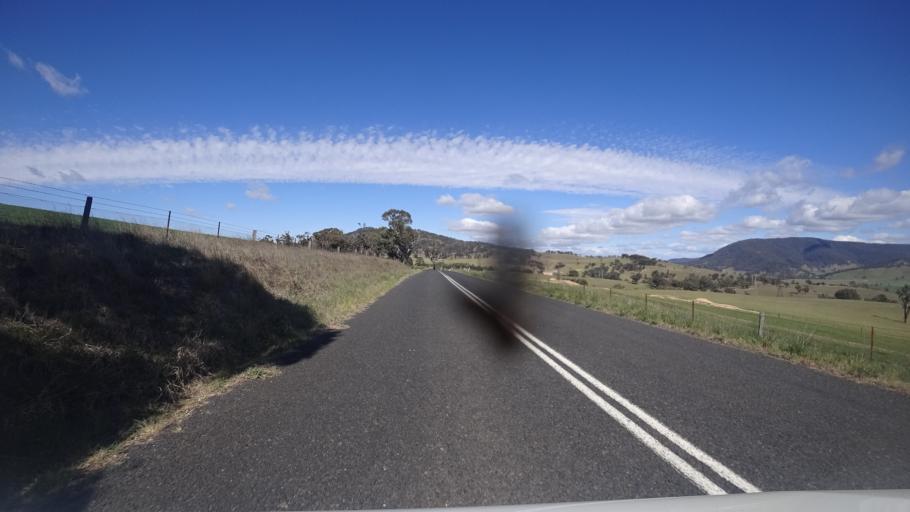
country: AU
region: New South Wales
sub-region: Lithgow
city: Portland
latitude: -33.5199
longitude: 149.9470
